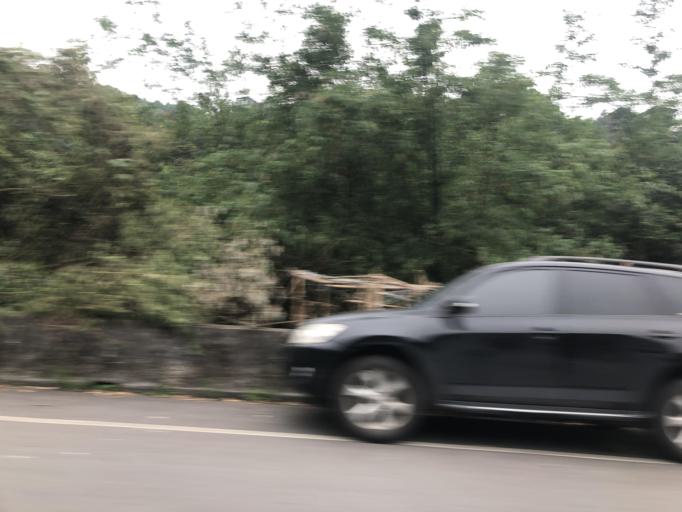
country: TW
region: Taiwan
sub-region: Keelung
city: Keelung
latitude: 25.1885
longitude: 121.6784
